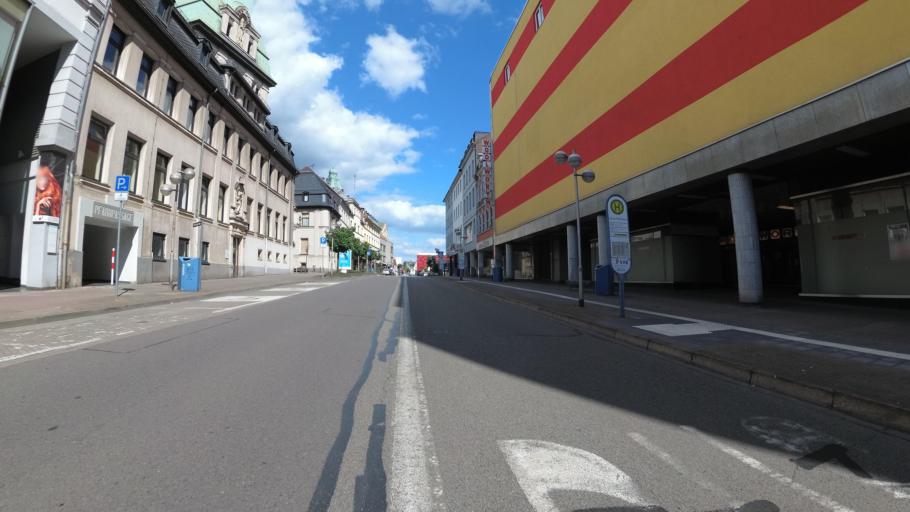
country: DE
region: Saarland
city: Volklingen
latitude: 49.2493
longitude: 6.8530
